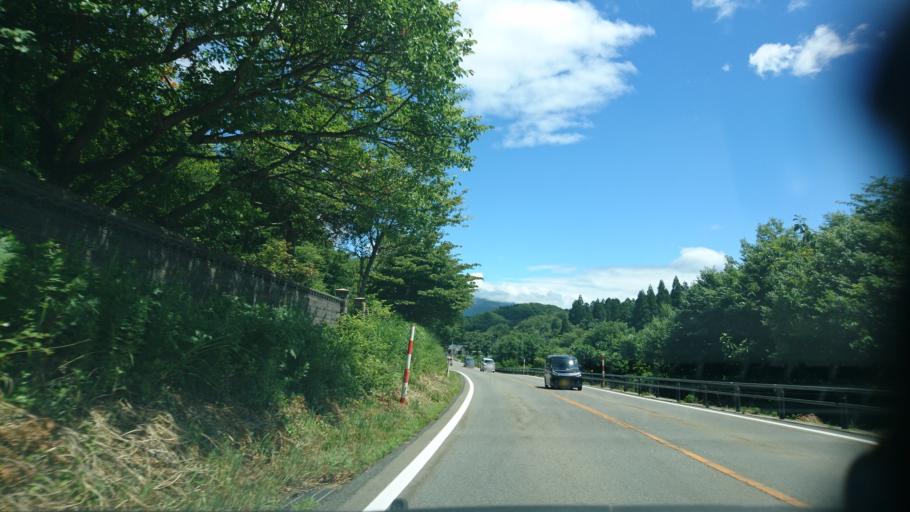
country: JP
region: Akita
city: Kakunodatemachi
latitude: 39.6666
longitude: 140.6896
